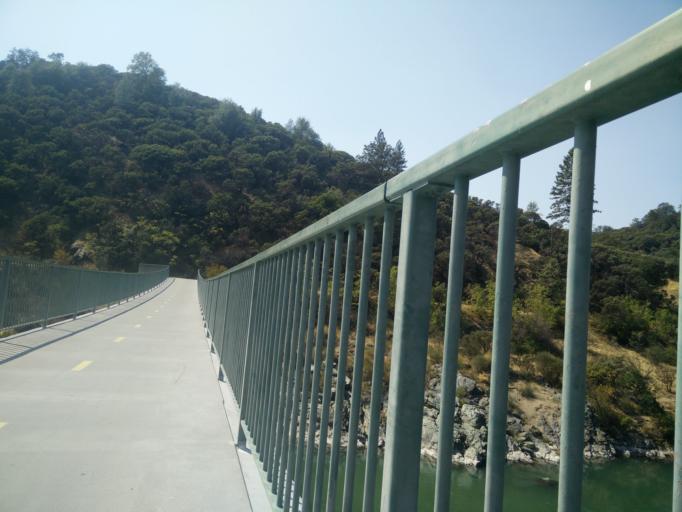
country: US
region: California
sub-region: Shasta County
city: Shasta
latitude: 40.6016
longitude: -122.4438
